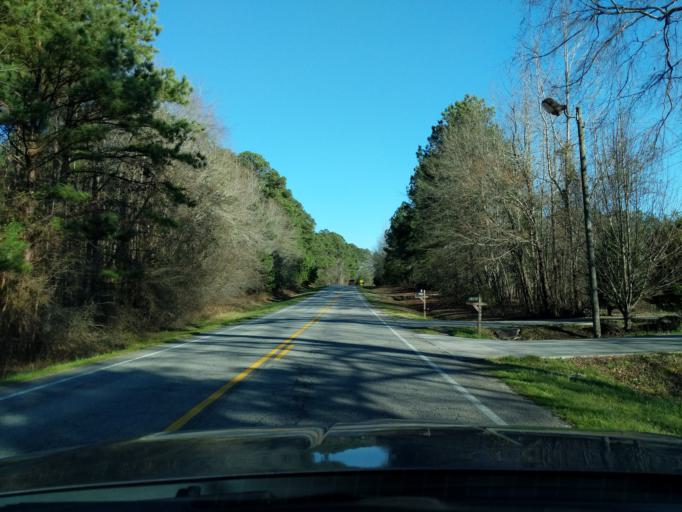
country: US
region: Georgia
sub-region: Columbia County
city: Grovetown
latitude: 33.4558
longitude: -82.2305
